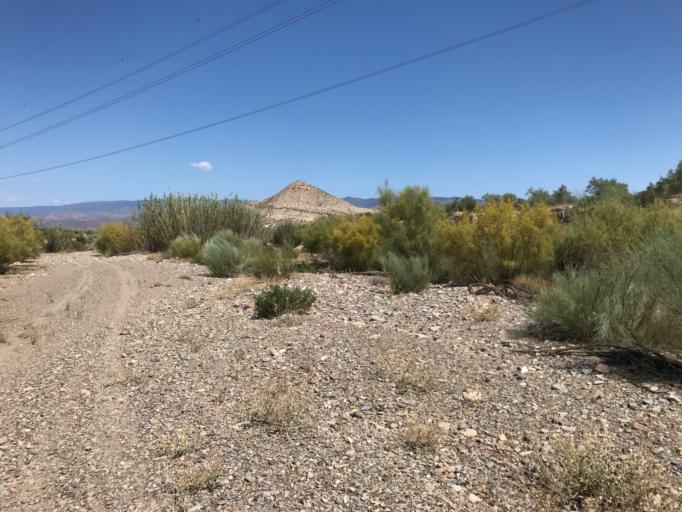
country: ES
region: Andalusia
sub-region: Provincia de Almeria
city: Turrillas
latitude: 37.0711
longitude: -2.2942
